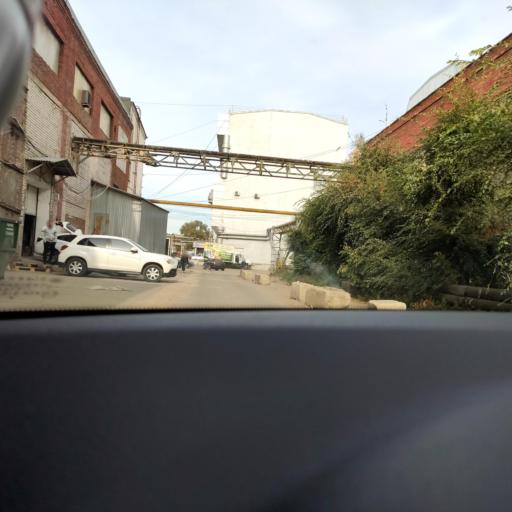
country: RU
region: Samara
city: Samara
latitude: 53.1934
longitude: 50.2467
